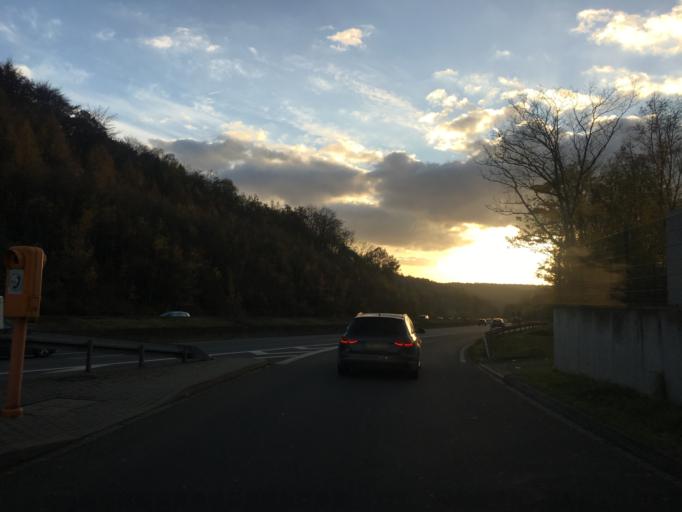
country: DE
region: North Rhine-Westphalia
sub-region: Regierungsbezirk Arnsberg
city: Schwelm
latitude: 51.2647
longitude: 7.2438
